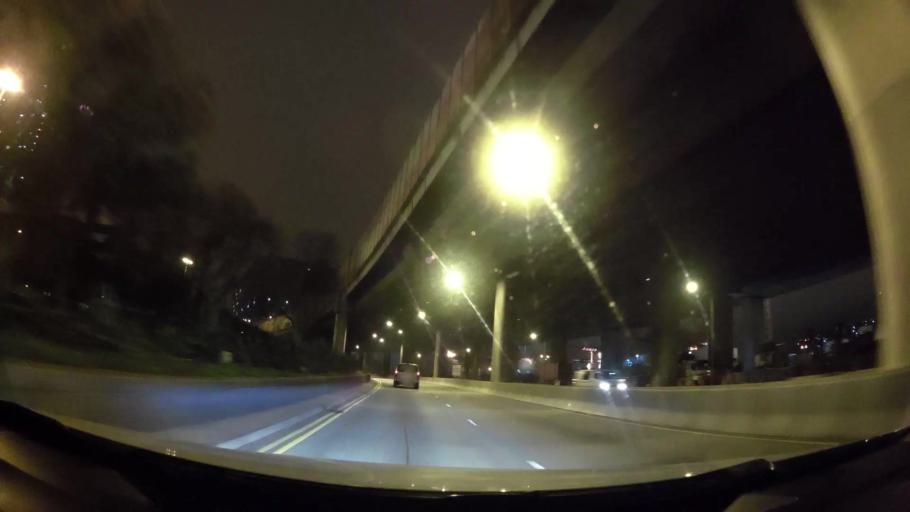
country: HK
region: Tsuen Wan
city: Tsuen Wan
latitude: 22.3480
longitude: 114.1247
